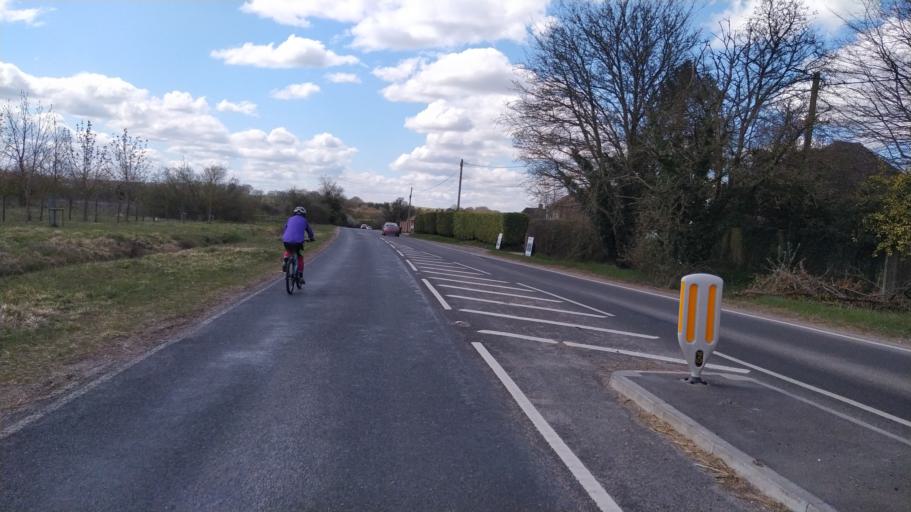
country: GB
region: England
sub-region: Hampshire
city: Abbotts Ann
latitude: 51.2128
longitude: -1.5713
